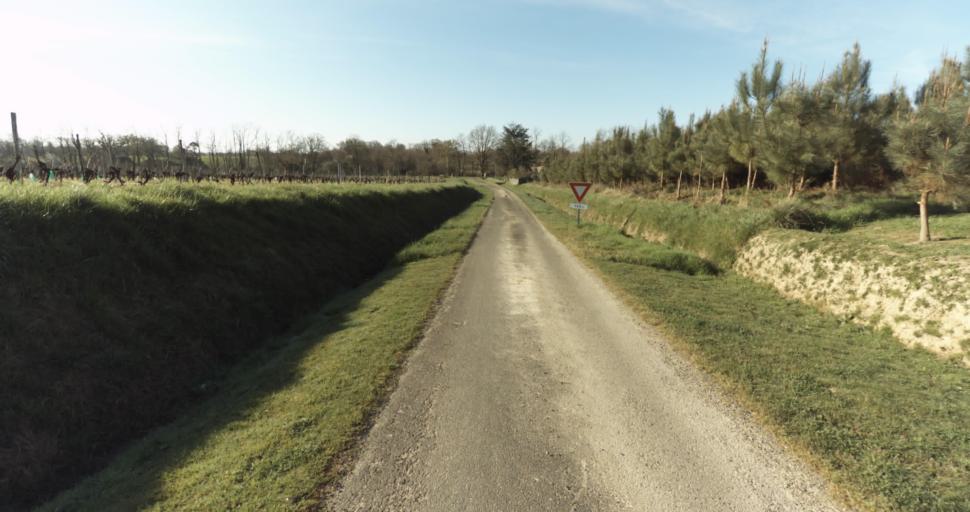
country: FR
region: Midi-Pyrenees
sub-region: Departement du Gers
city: Cazaubon
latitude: 43.9901
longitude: -0.1464
